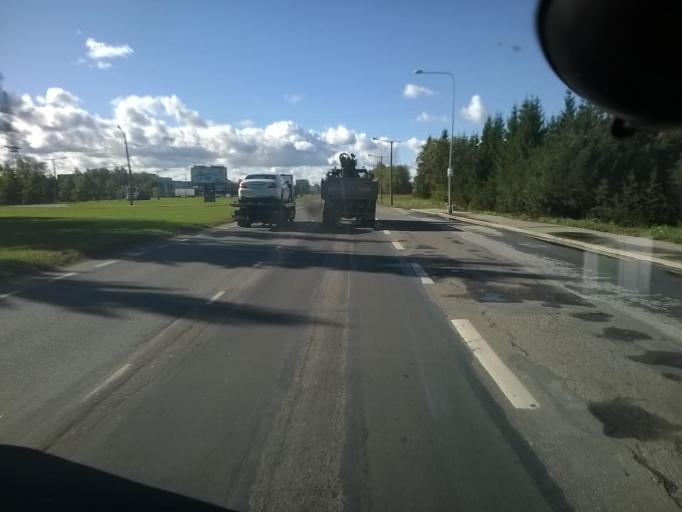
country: EE
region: Harju
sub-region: Tallinna linn
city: Kose
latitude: 59.4355
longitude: 24.8692
